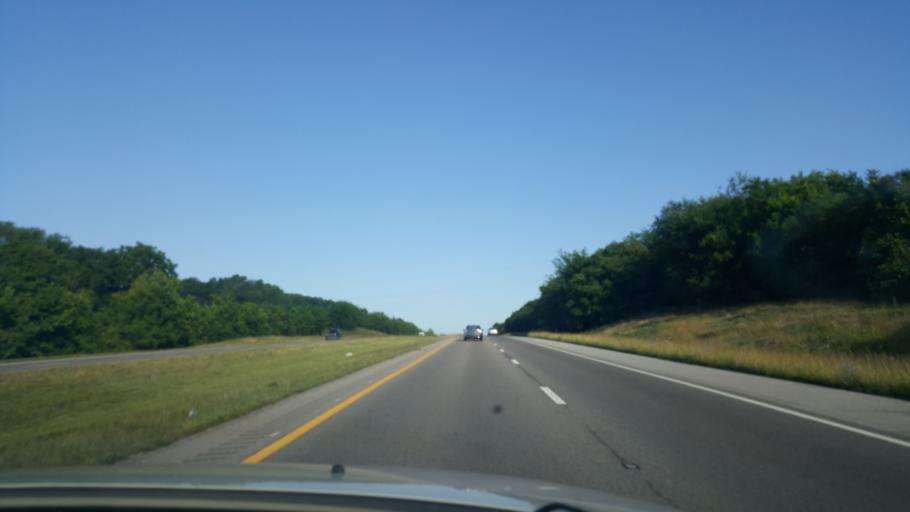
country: US
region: Tennessee
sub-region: Maury County
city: Columbia
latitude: 35.6288
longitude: -87.0906
